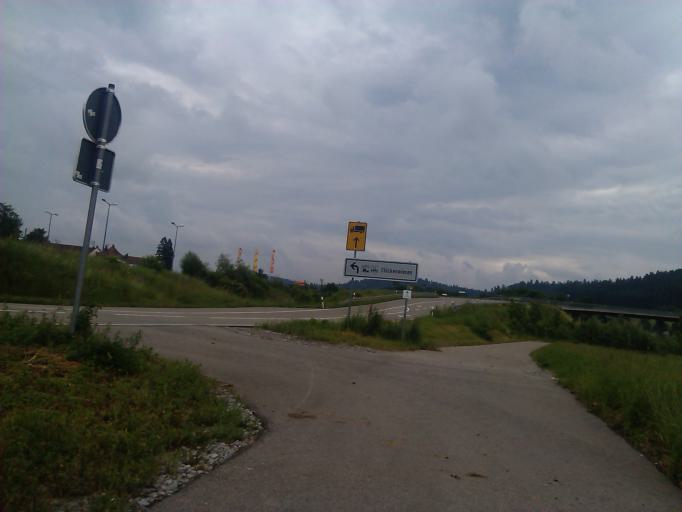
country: DE
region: Baden-Wuerttemberg
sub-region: Regierungsbezirk Stuttgart
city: Fichtenberg
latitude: 48.9895
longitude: 9.6937
